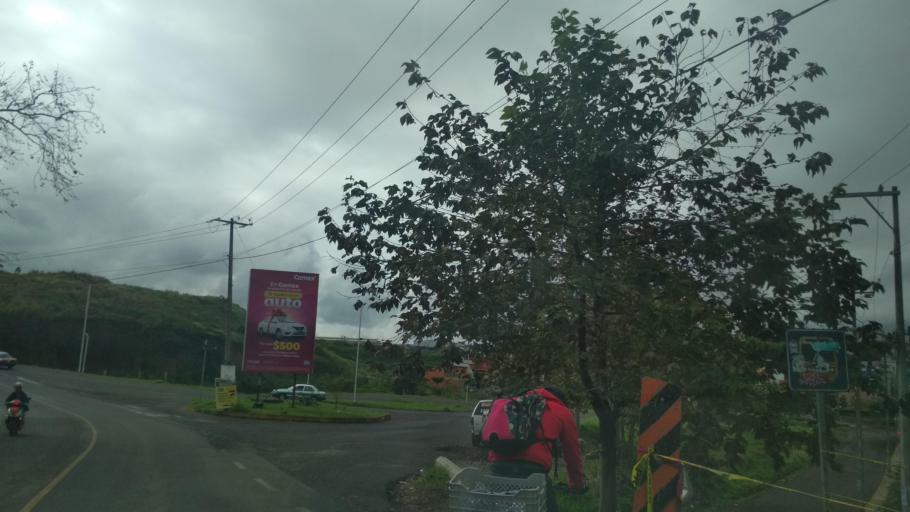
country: MX
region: Veracruz
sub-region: Emiliano Zapata
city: Las Trancas
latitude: 19.5043
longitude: -96.8620
